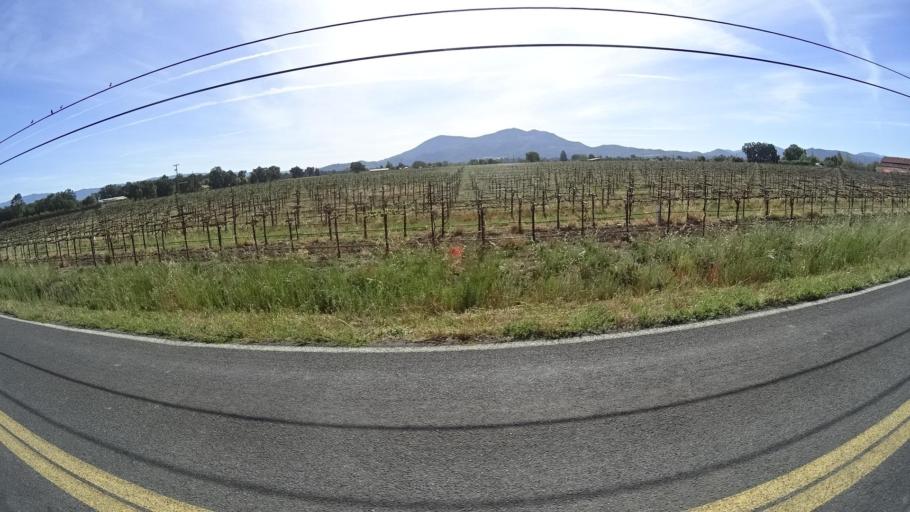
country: US
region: California
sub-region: Lake County
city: Kelseyville
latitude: 38.9856
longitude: -122.8943
